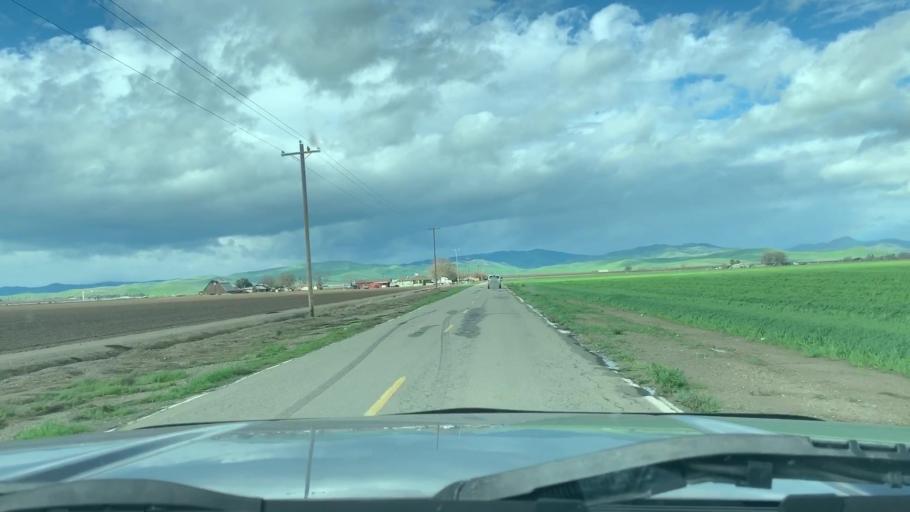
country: US
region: California
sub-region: Merced County
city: Gustine
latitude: 37.1223
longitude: -120.9934
